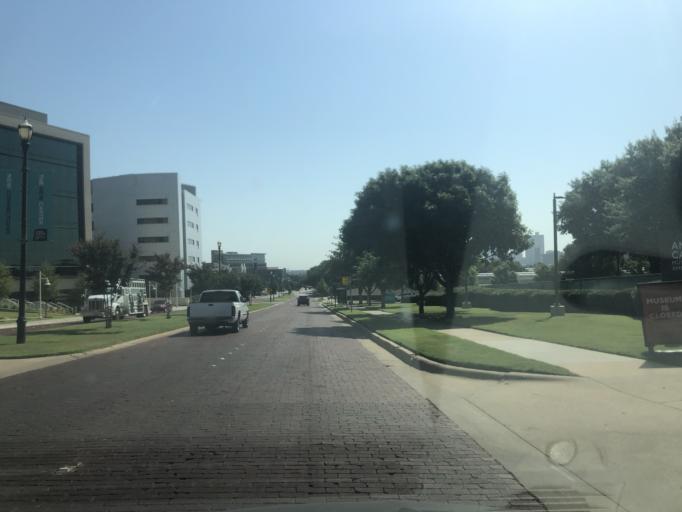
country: US
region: Texas
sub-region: Tarrant County
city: River Oaks
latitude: 32.7484
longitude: -97.3680
